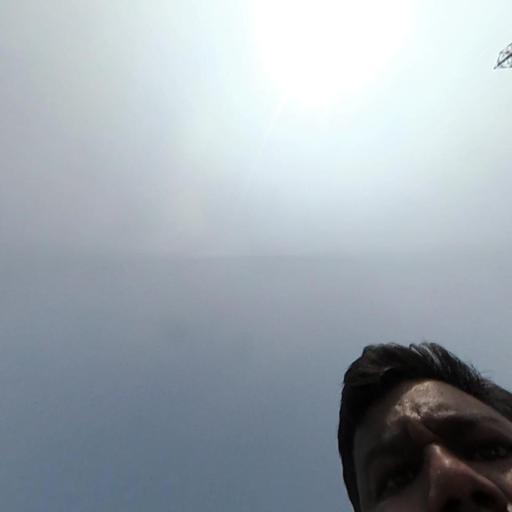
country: IN
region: Telangana
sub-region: Nalgonda
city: Nalgonda
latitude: 17.1828
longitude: 79.1250
